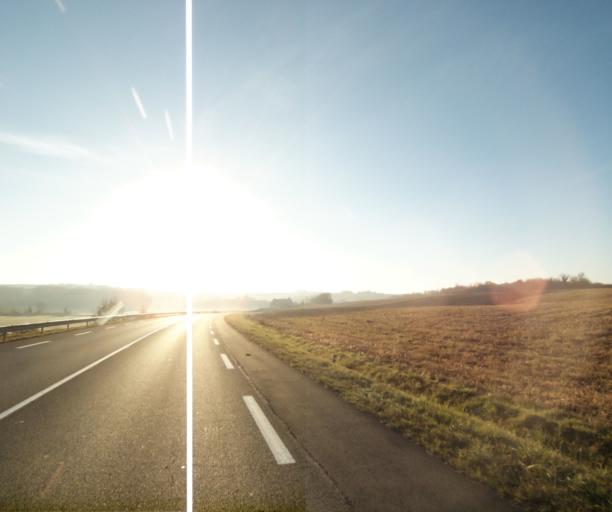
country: FR
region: Poitou-Charentes
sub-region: Departement de la Charente-Maritime
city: Chaniers
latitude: 45.7236
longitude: -0.4981
